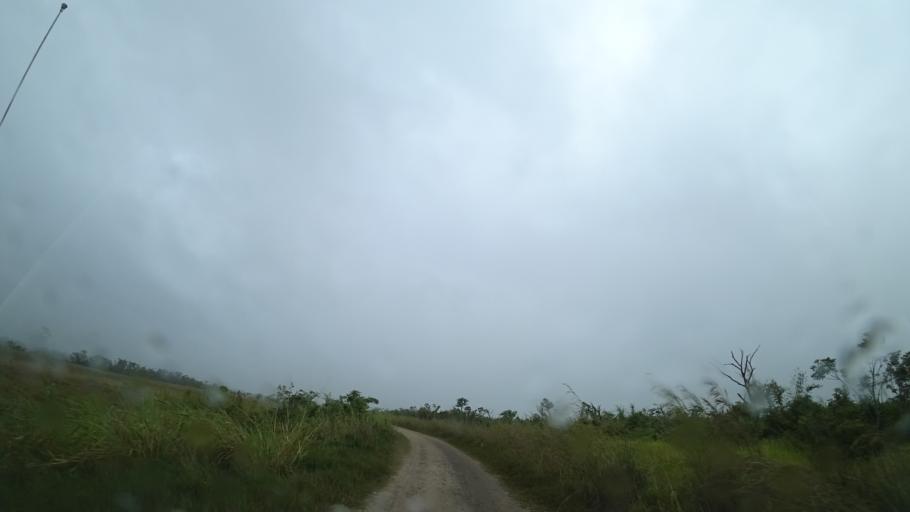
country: MZ
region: Sofala
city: Dondo
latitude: -19.5773
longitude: 35.1124
